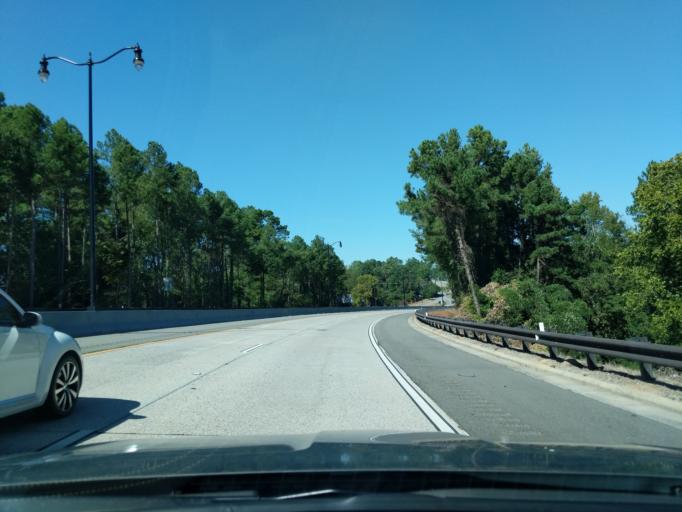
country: US
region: Georgia
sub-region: Richmond County
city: Augusta
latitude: 33.4894
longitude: -82.0097
